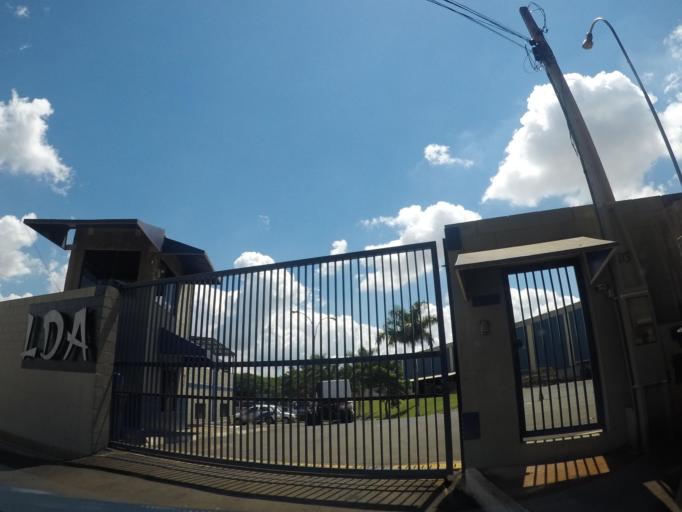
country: BR
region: Sao Paulo
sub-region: Hortolandia
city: Hortolandia
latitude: -22.8242
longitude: -47.2001
